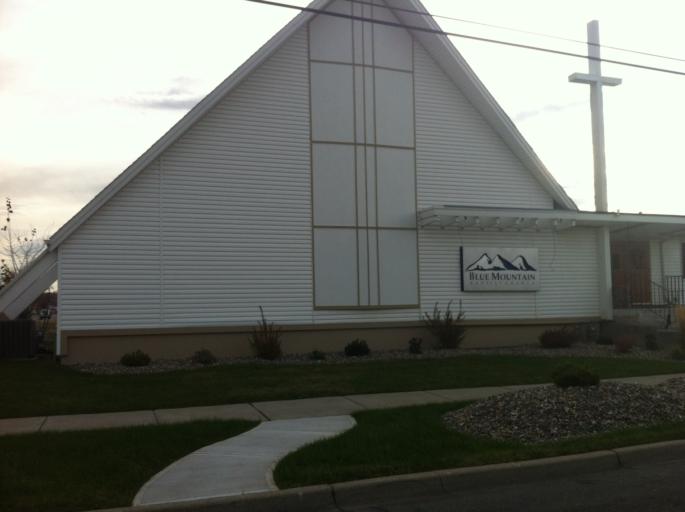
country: US
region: Oregon
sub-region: Baker County
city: Baker City
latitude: 44.7861
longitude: -117.8388
